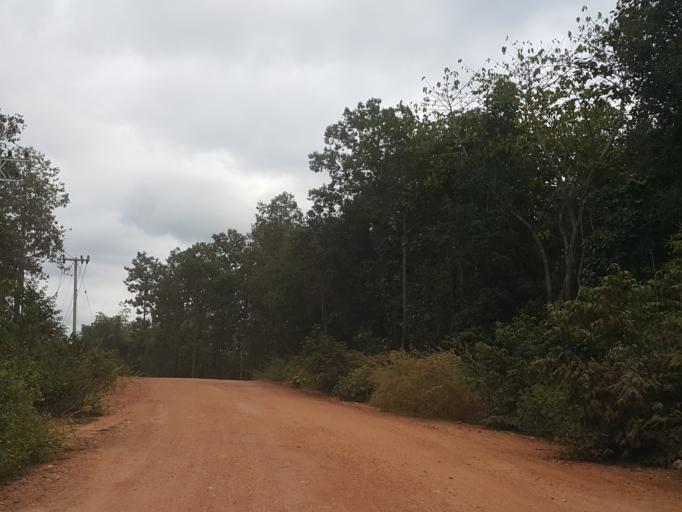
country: TH
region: Lampang
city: Chae Hom
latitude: 18.5792
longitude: 99.4512
